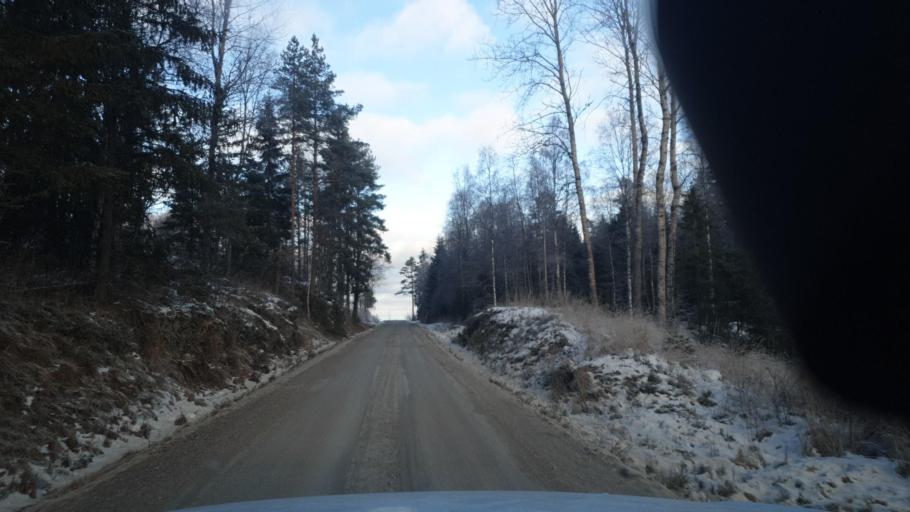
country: SE
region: Vaermland
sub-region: Eda Kommun
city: Charlottenberg
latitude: 60.0291
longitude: 12.5120
